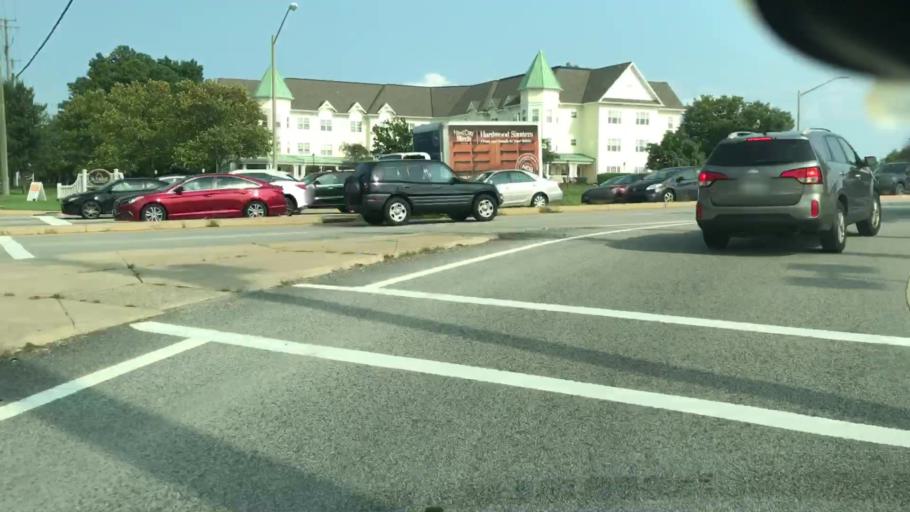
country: US
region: Virginia
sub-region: Fairfax County
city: Springfield
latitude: 38.7777
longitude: -77.1722
